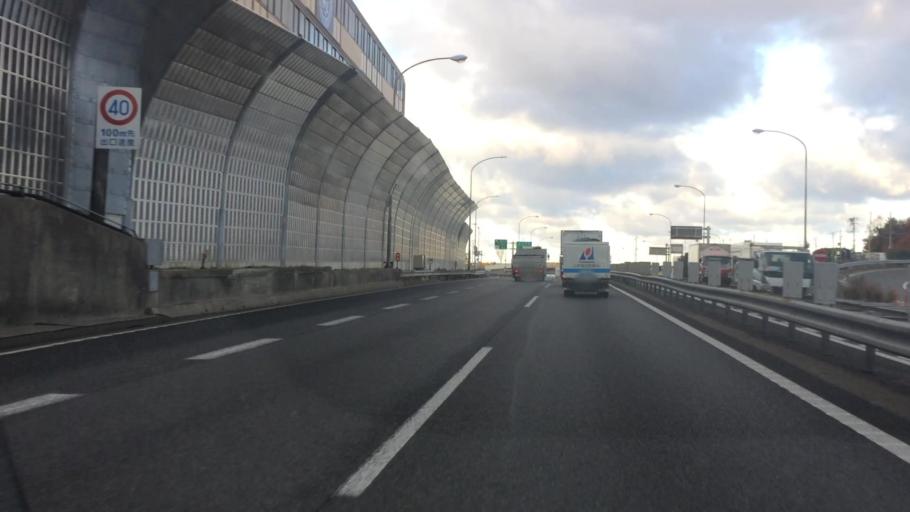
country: JP
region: Hyogo
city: Akashi
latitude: 34.6471
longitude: 135.0554
